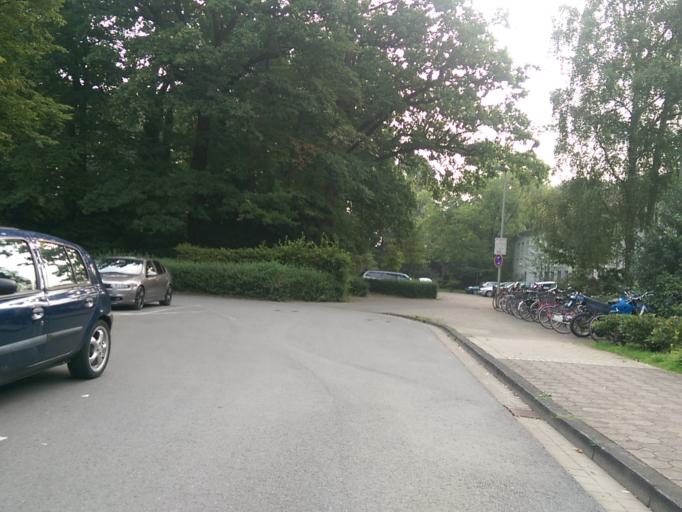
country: DE
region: North Rhine-Westphalia
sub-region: Regierungsbezirk Detmold
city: Guetersloh
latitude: 51.9035
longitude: 8.3680
